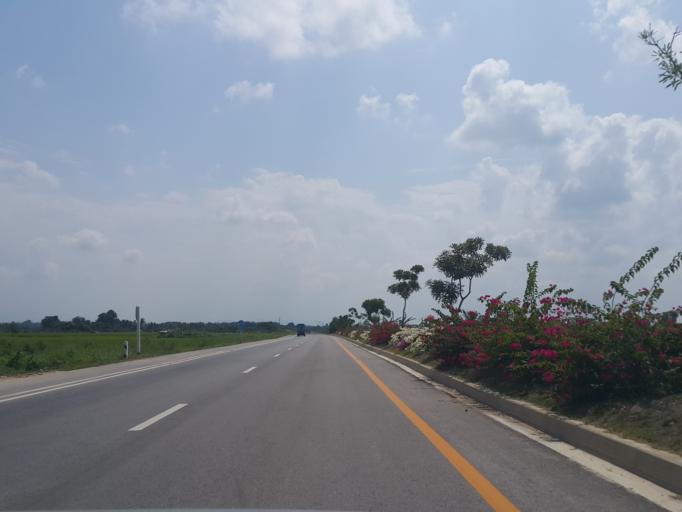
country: TH
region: Chiang Mai
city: San Pa Tong
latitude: 18.5776
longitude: 98.8443
